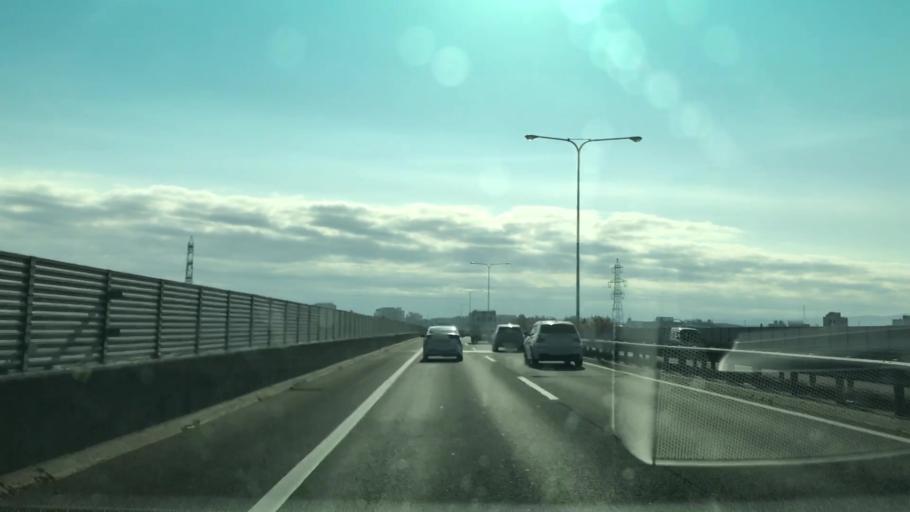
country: JP
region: Hokkaido
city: Sapporo
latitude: 43.0380
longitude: 141.4410
